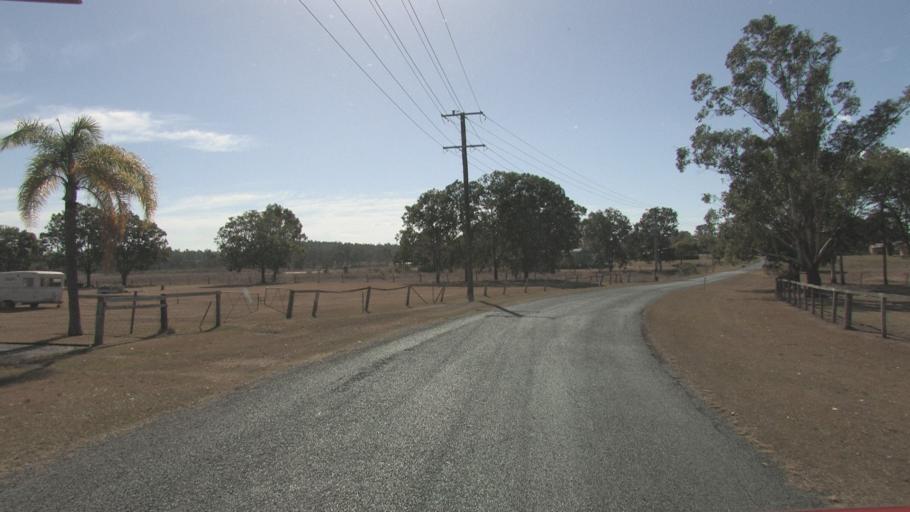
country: AU
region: Queensland
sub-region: Logan
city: Cedar Vale
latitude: -27.8541
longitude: 152.9763
